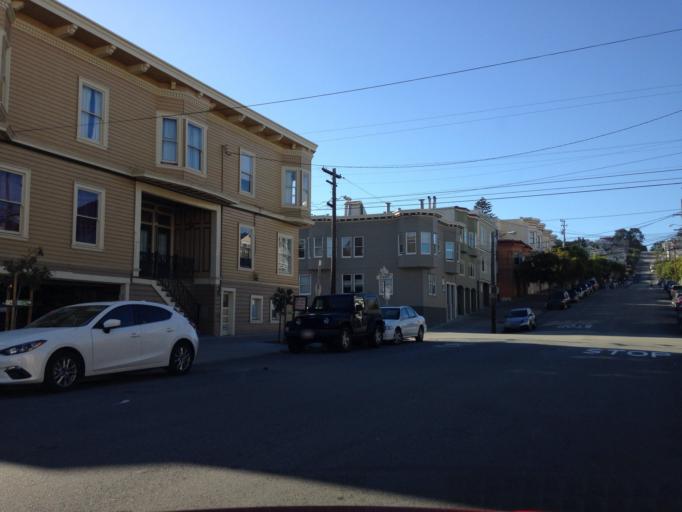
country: US
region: California
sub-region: San Francisco County
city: San Francisco
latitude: 37.7505
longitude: -122.4295
